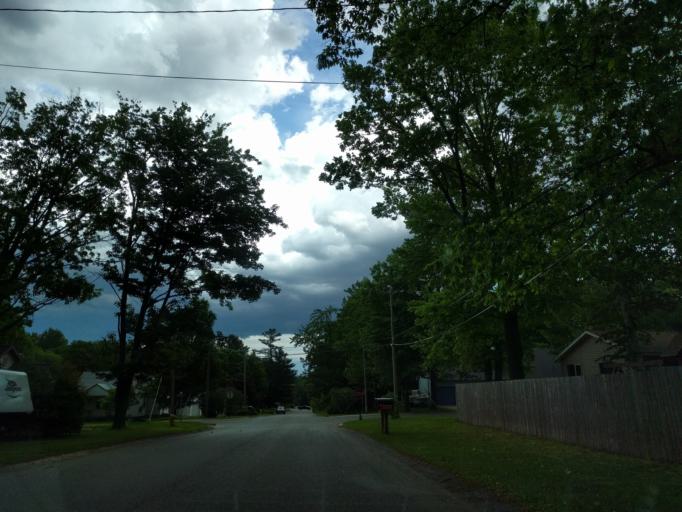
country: US
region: Michigan
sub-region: Marquette County
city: Trowbridge Park
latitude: 46.5543
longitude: -87.4408
